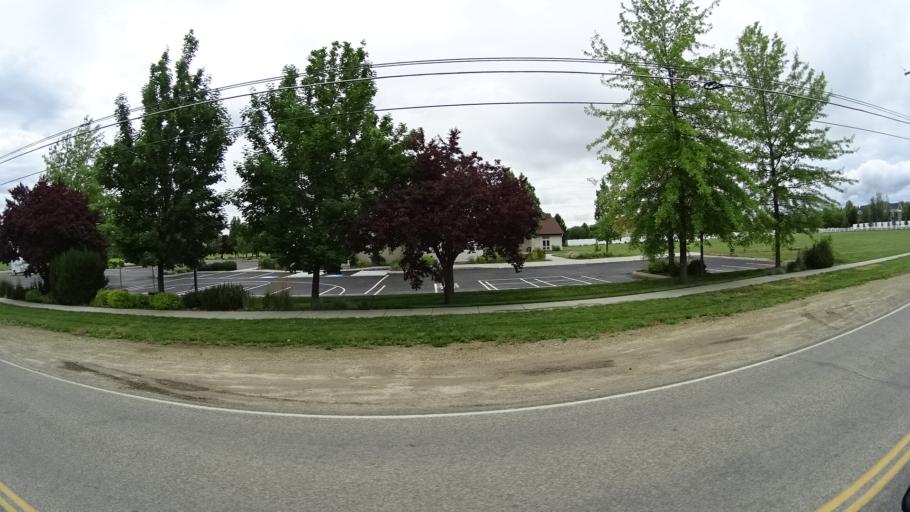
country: US
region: Idaho
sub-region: Ada County
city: Eagle
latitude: 43.7062
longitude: -116.4028
